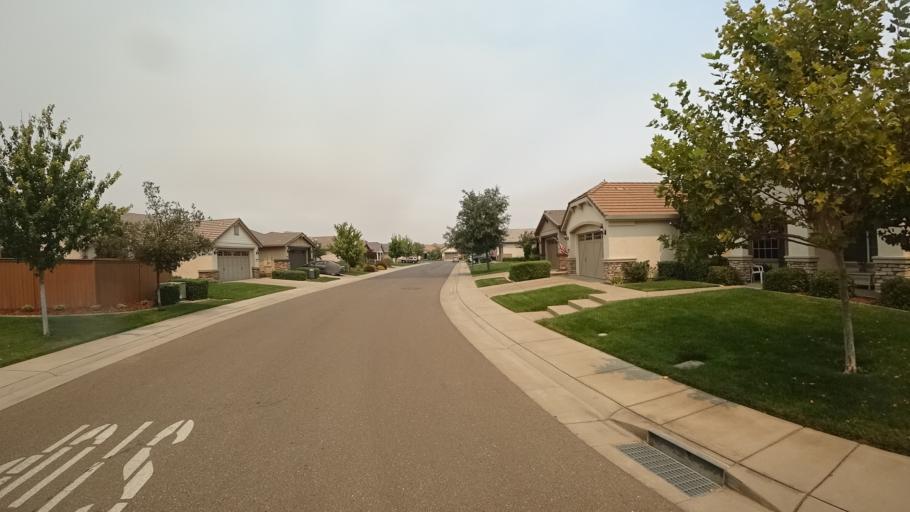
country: US
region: California
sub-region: Sacramento County
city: Laguna
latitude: 38.3988
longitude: -121.4141
